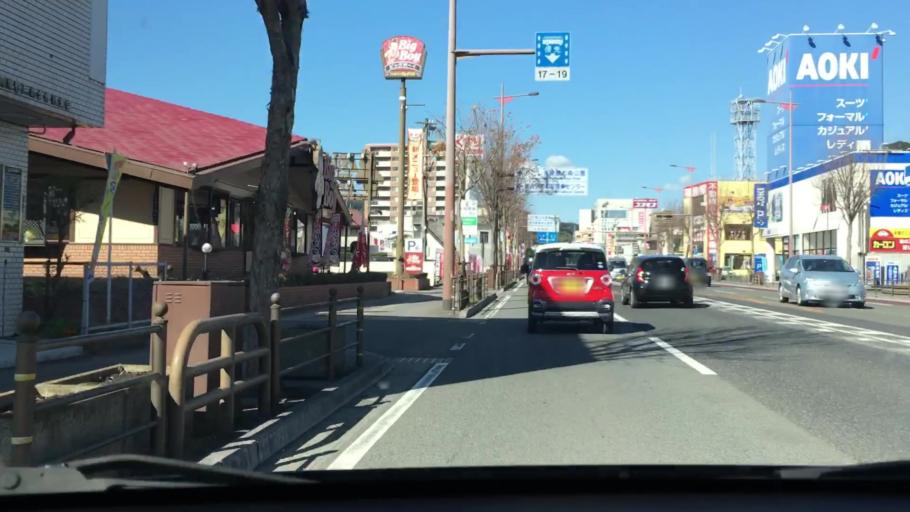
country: JP
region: Kagoshima
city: Kagoshima-shi
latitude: 31.6131
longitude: 130.5315
